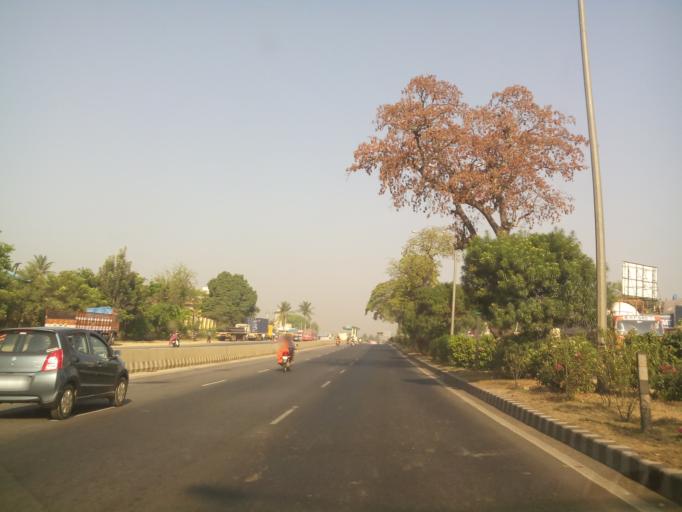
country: IN
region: Karnataka
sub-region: Bangalore Rural
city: Nelamangala
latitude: 13.0789
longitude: 77.4272
